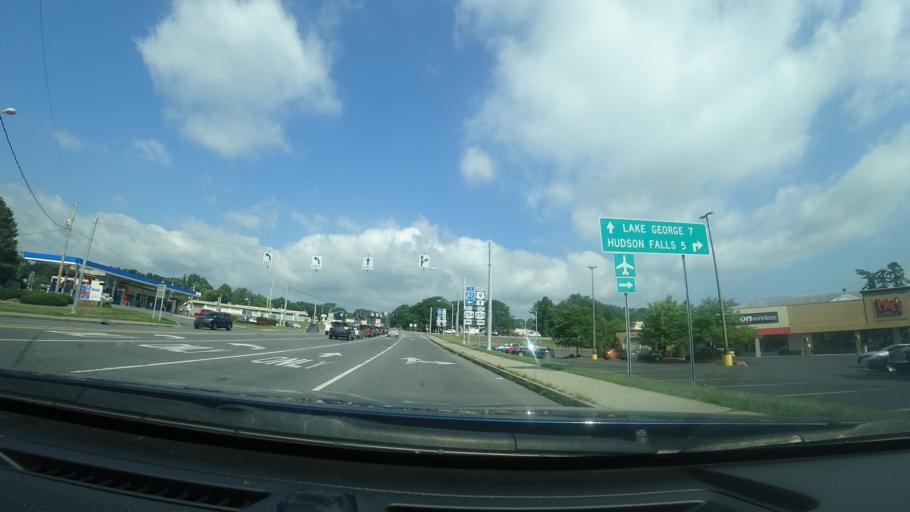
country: US
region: New York
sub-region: Warren County
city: Glens Falls North
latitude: 43.3297
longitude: -73.6717
